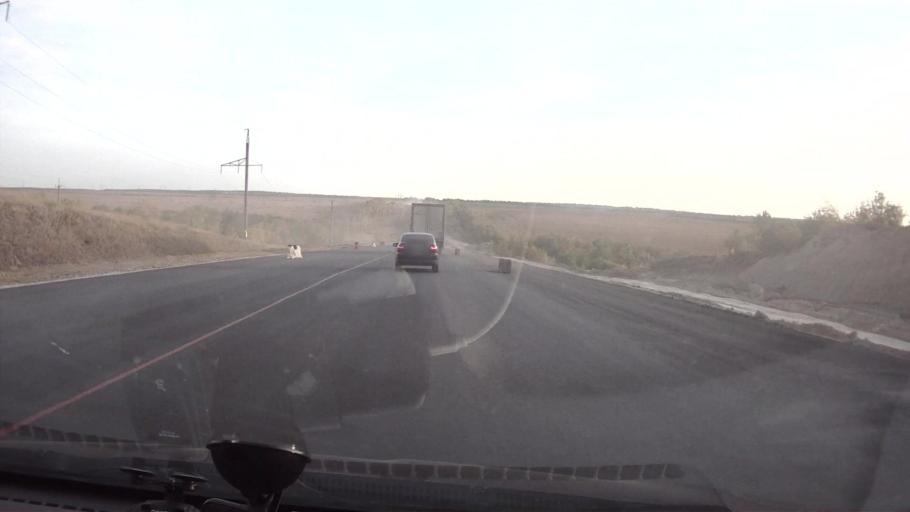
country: RU
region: Saratov
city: Krasnoarmeysk
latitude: 51.2267
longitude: 45.6481
